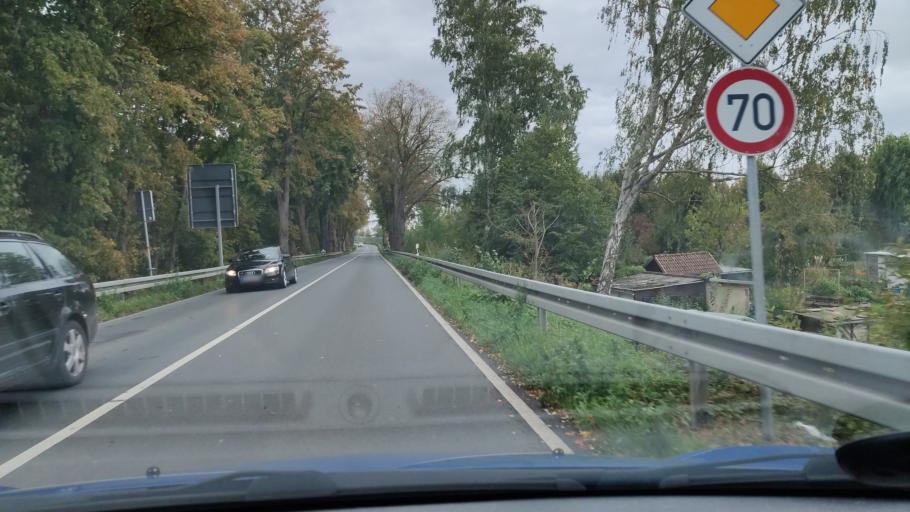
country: DE
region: Lower Saxony
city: Seelze
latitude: 52.3900
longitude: 9.5848
